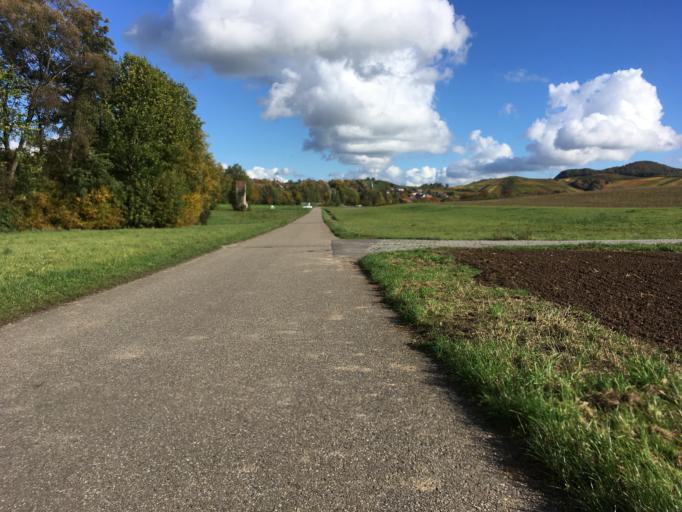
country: DE
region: Baden-Wuerttemberg
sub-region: Regierungsbezirk Stuttgart
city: Pfedelbach
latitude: 49.1734
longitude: 9.5440
